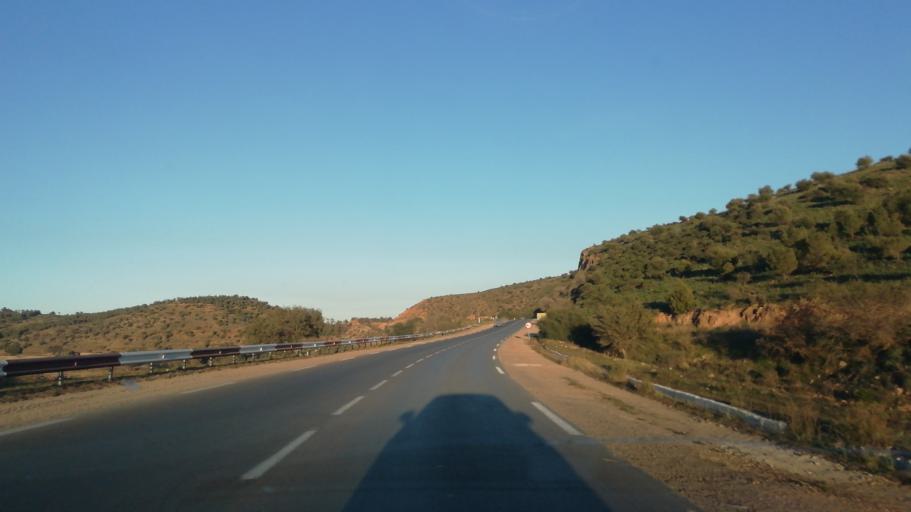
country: DZ
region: Tlemcen
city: Nedroma
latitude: 34.8659
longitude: -1.6767
